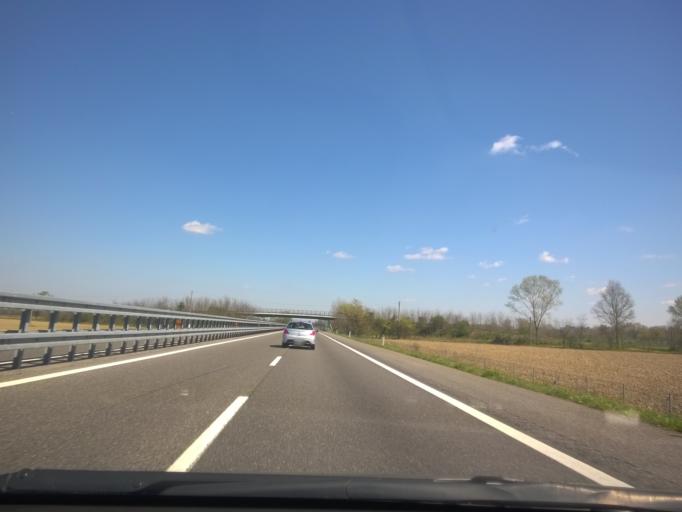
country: IT
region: Lombardy
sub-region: Provincia di Pavia
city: Arena Po
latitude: 45.0840
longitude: 9.3428
